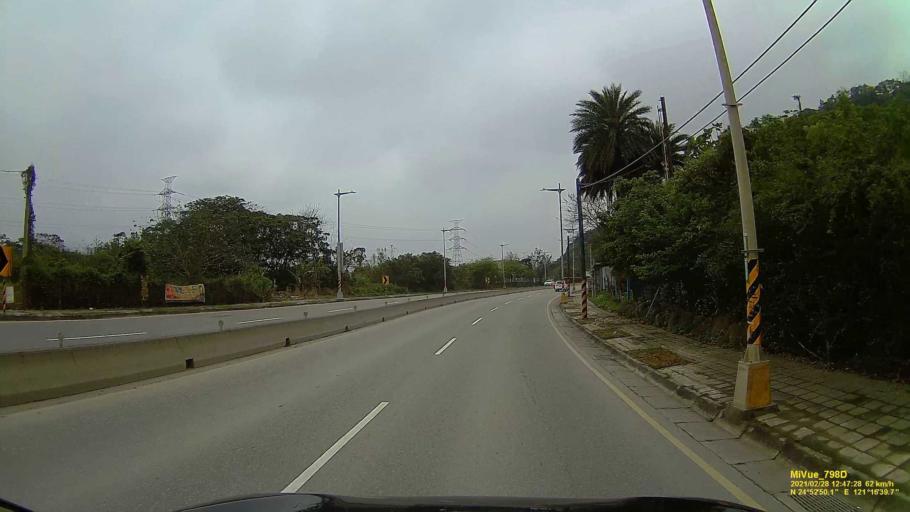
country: TW
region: Taiwan
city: Daxi
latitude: 24.8804
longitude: 121.2777
